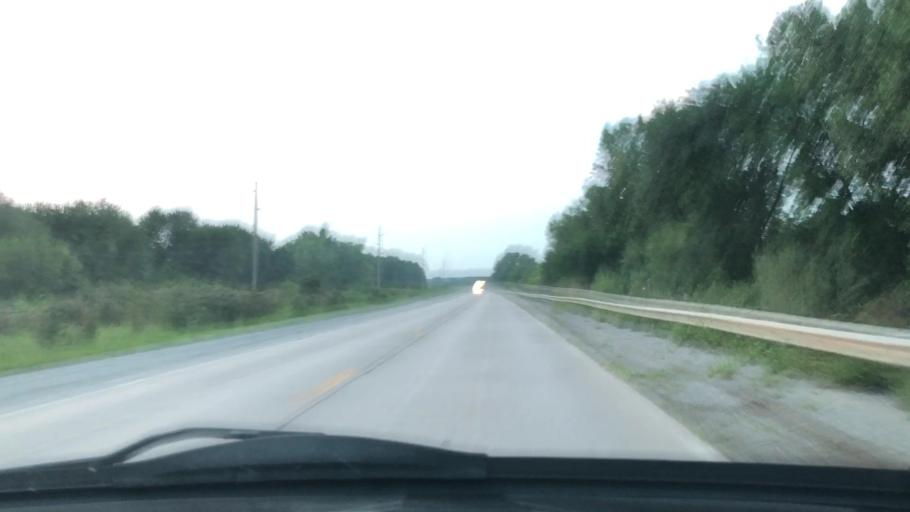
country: US
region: Iowa
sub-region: Johnson County
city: North Liberty
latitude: 41.7898
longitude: -91.6384
